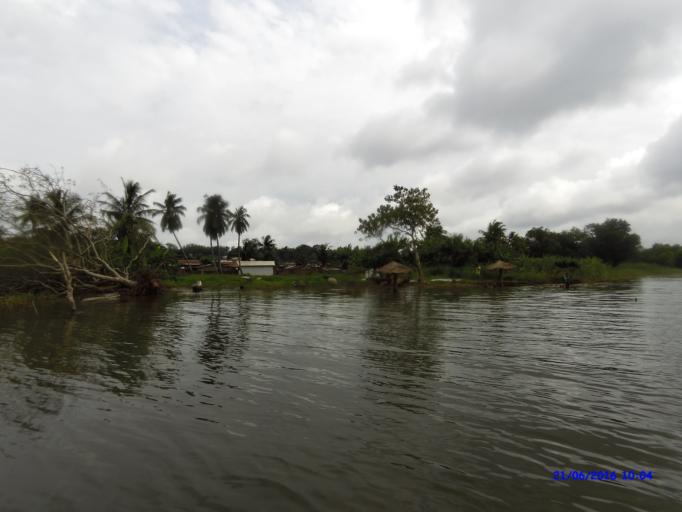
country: BJ
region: Mono
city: Come
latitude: 6.4561
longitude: 1.9255
